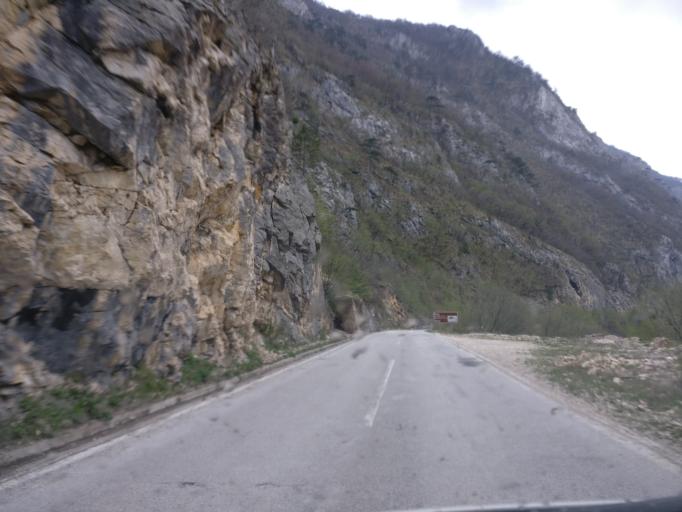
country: ME
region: Opstina Pluzine
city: Pluzine
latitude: 43.2114
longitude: 18.8587
